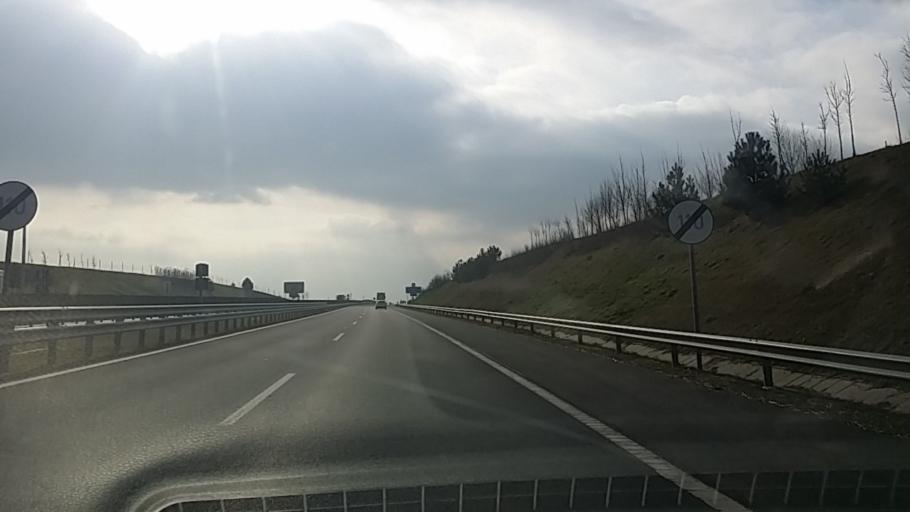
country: HU
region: Tolna
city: Bataszek
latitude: 46.1438
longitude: 18.6333
